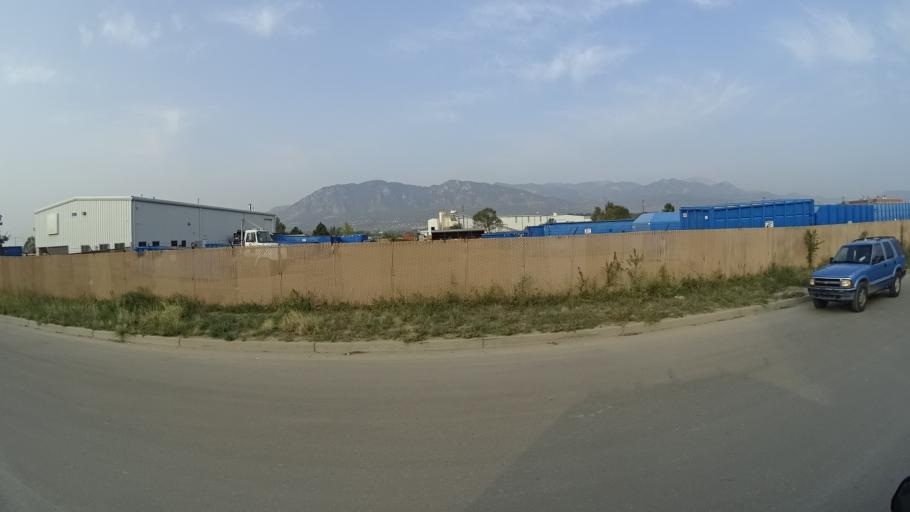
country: US
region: Colorado
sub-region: El Paso County
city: Stratmoor
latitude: 38.7804
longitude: -104.7715
